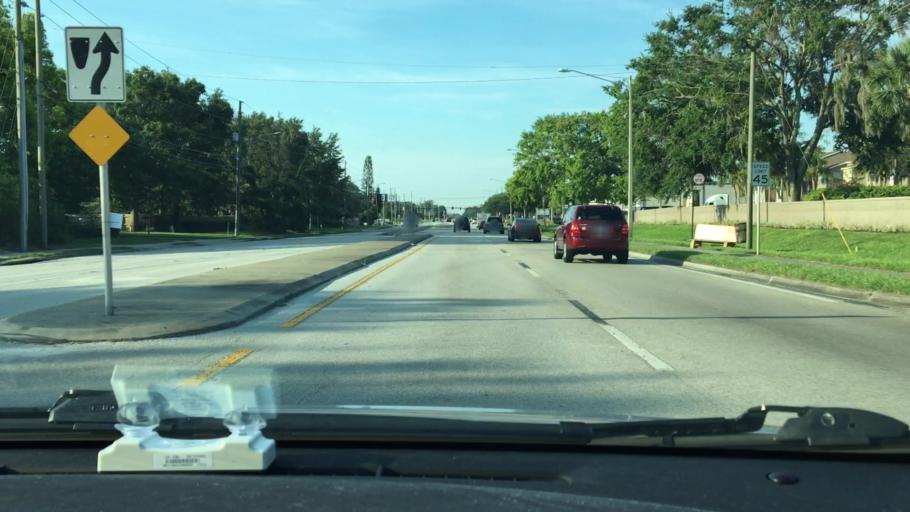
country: US
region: Florida
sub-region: Seminole County
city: Goldenrod
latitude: 28.6014
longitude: -81.2867
